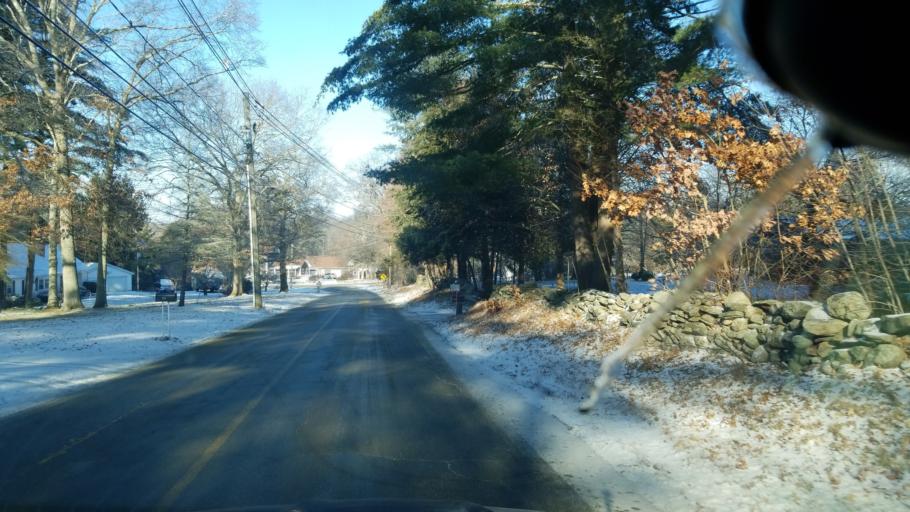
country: US
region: Connecticut
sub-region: Windham County
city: East Brooklyn
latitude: 41.8118
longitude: -71.9074
